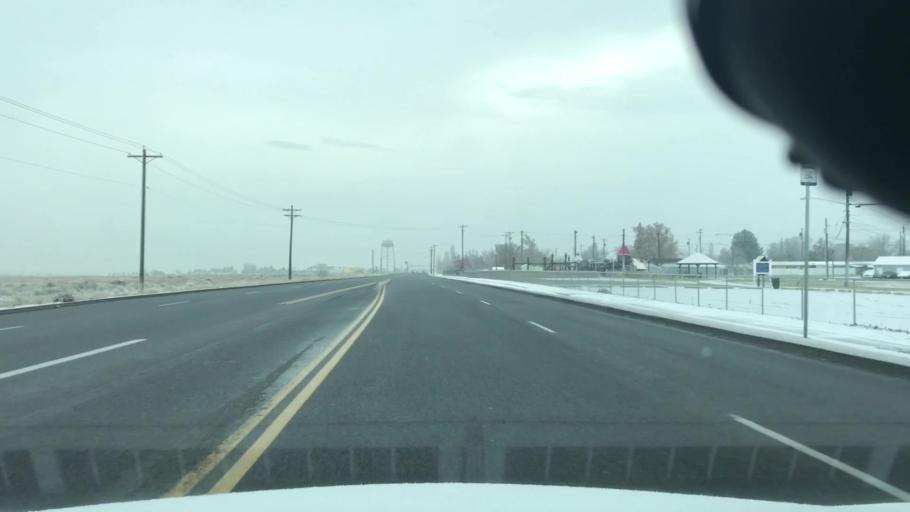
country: US
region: Washington
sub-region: Grant County
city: Moses Lake North
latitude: 47.1707
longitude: -119.3174
